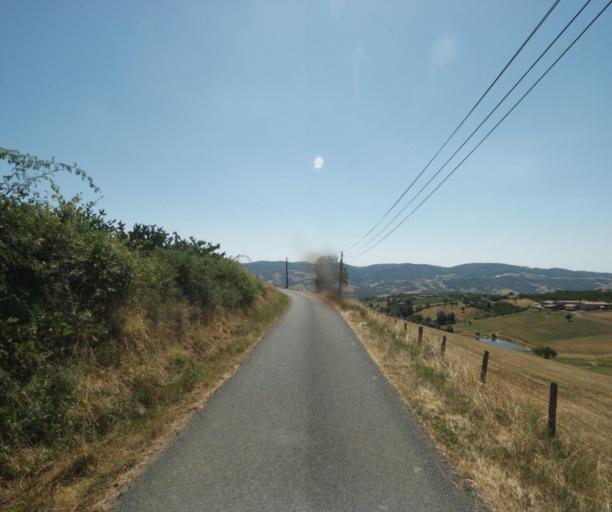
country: FR
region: Rhone-Alpes
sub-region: Departement du Rhone
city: Bessenay
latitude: 45.7850
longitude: 4.5284
